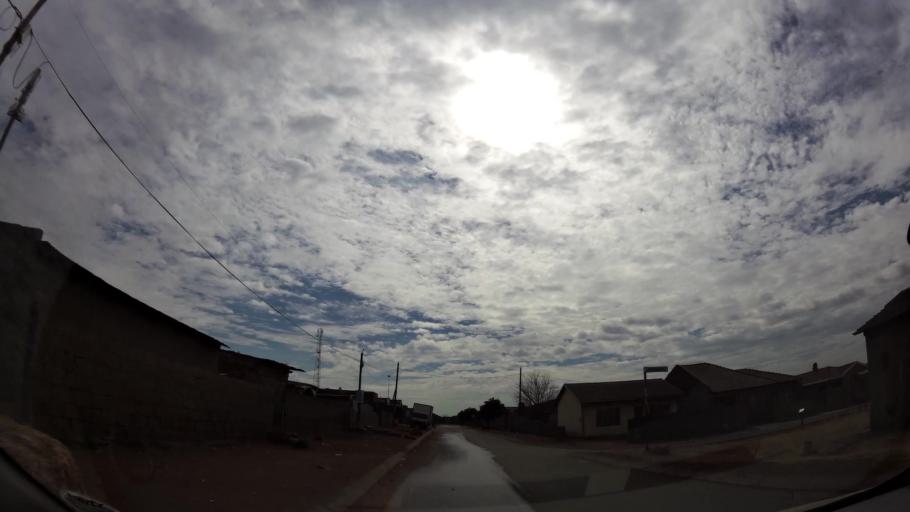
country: ZA
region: Gauteng
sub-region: Ekurhuleni Metropolitan Municipality
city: Germiston
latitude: -26.3772
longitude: 28.1658
